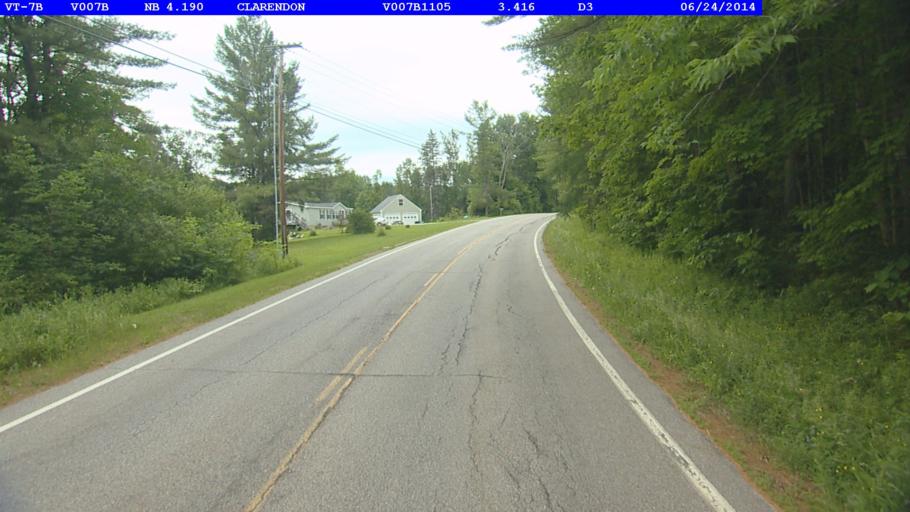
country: US
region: Vermont
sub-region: Rutland County
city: Rutland
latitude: 43.5478
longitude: -72.9576
